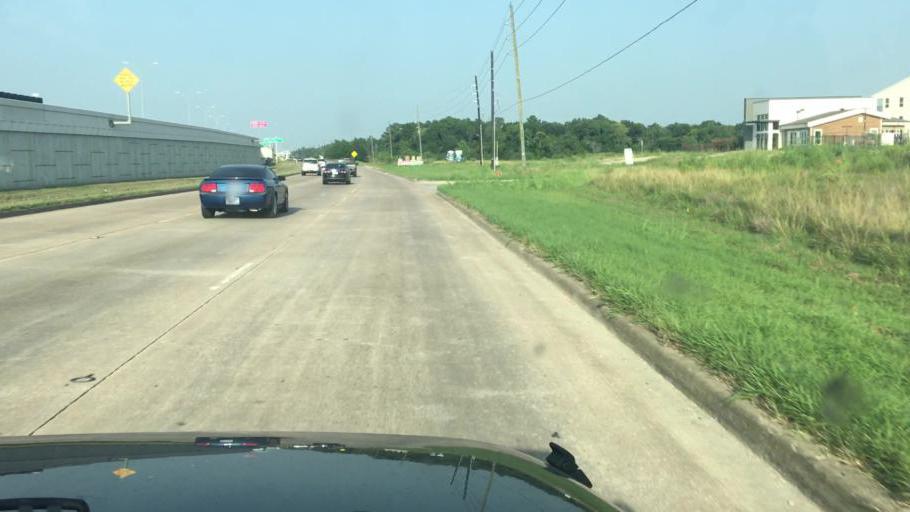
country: US
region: Texas
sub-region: Harris County
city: Humble
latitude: 29.9339
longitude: -95.2378
